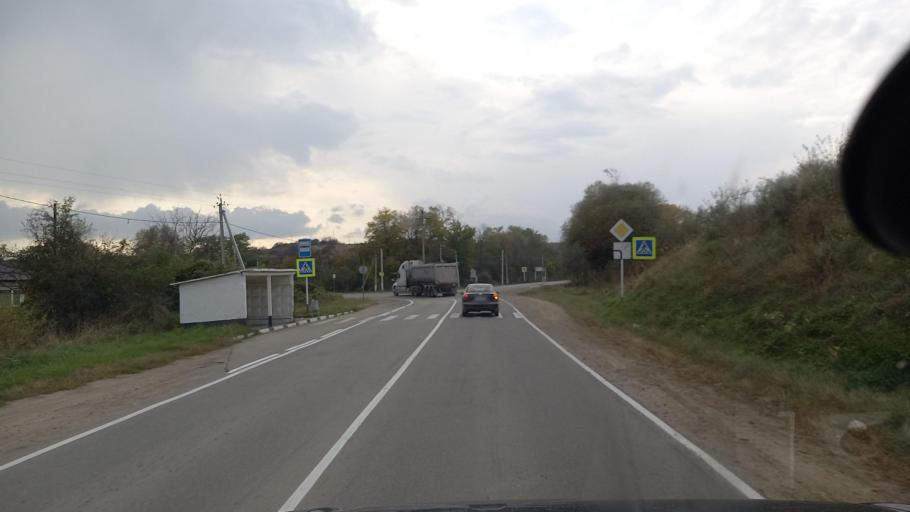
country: RU
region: Krasnodarskiy
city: Mostovskoy
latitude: 44.3887
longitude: 40.7409
